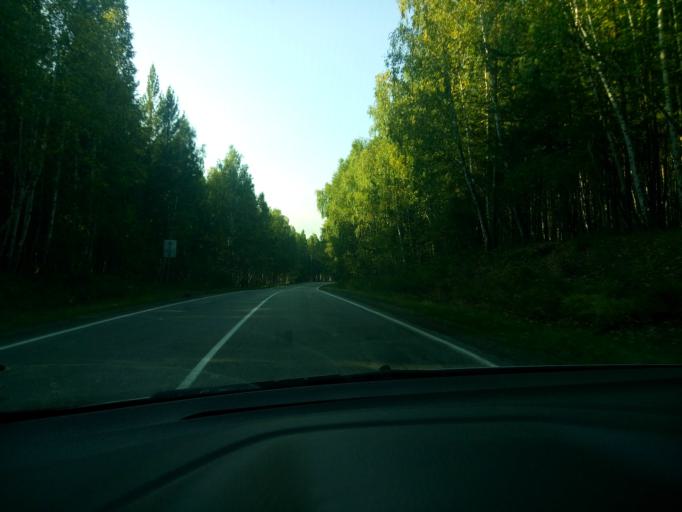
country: RU
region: Chelyabinsk
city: Ozersk
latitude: 55.8468
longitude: 60.6563
